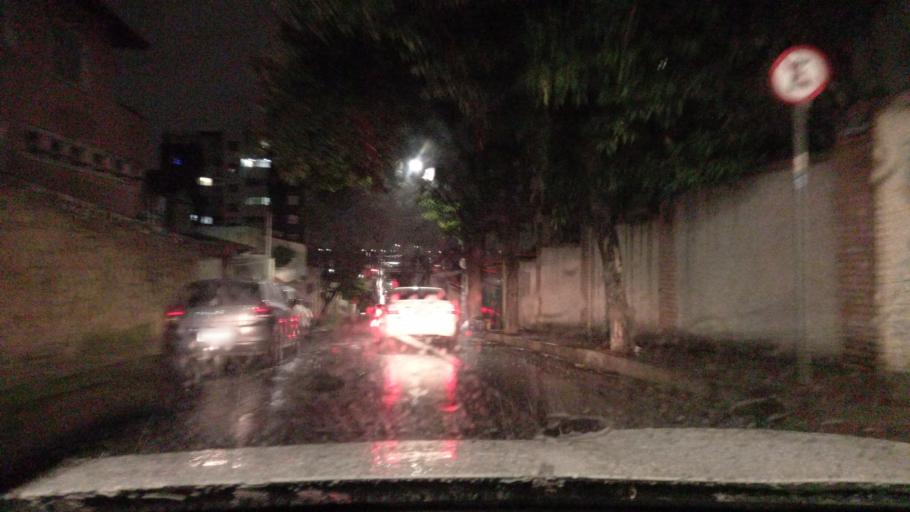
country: BR
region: Minas Gerais
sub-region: Belo Horizonte
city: Belo Horizonte
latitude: -19.9052
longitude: -43.9725
